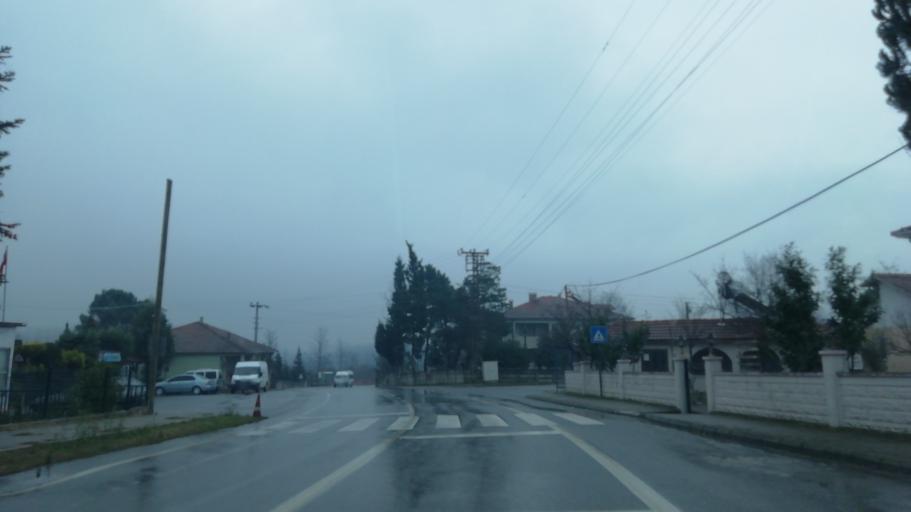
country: TR
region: Sakarya
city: Karapurcek
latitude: 40.6783
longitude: 30.5525
